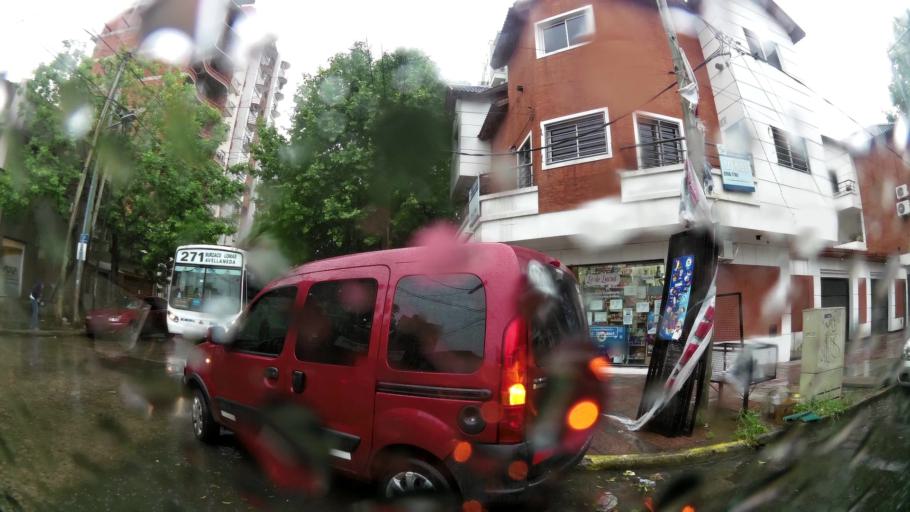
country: AR
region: Buenos Aires
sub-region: Partido de Lanus
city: Lanus
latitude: -34.7114
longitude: -58.3947
